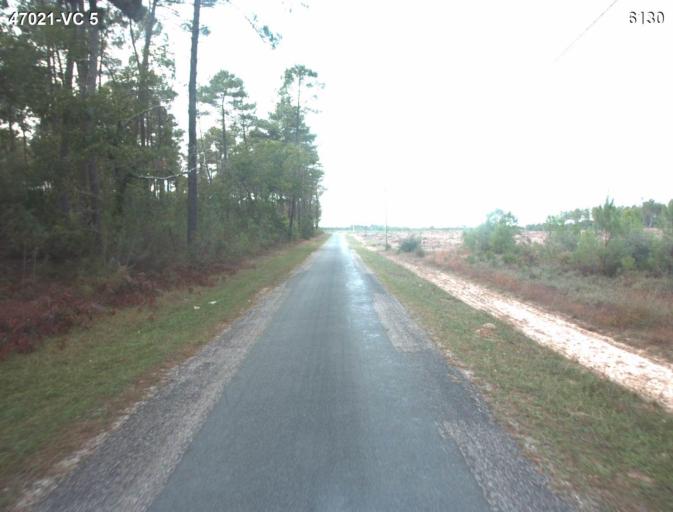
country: FR
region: Aquitaine
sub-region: Departement du Lot-et-Garonne
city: Barbaste
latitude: 44.1500
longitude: 0.2248
